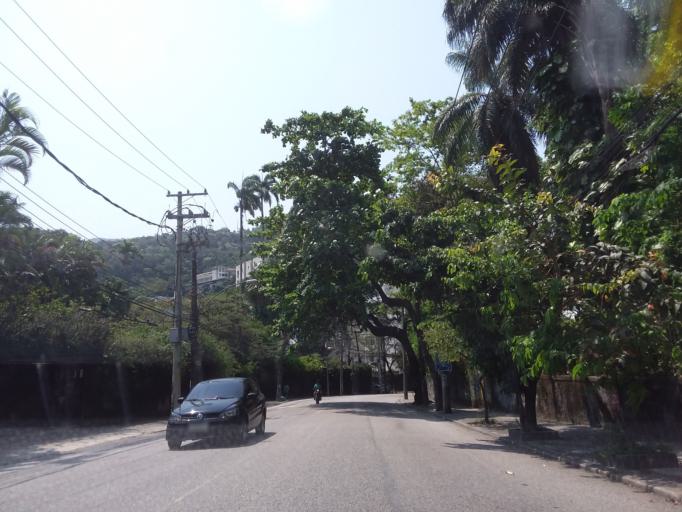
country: BR
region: Rio de Janeiro
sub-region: Rio De Janeiro
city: Rio de Janeiro
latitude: -22.9796
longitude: -43.2346
